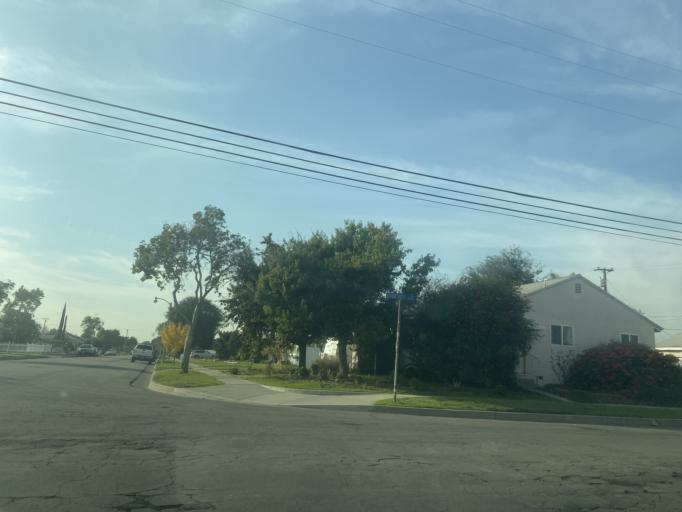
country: US
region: California
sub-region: Orange County
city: Buena Park
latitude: 33.8616
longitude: -117.9636
